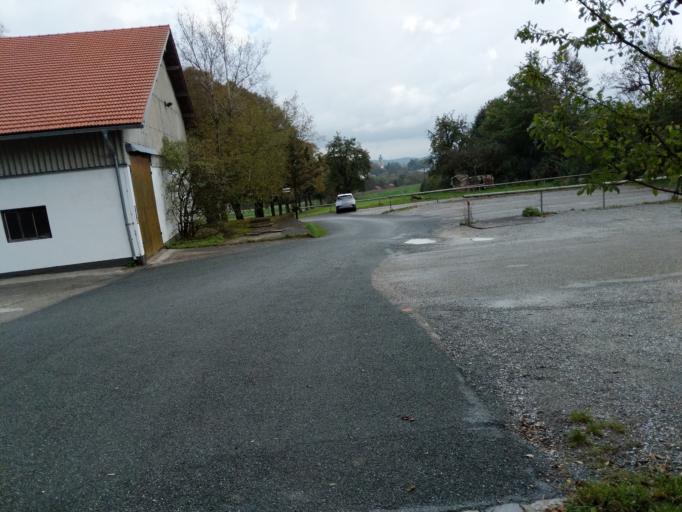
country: DE
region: Bavaria
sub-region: Upper Bavaria
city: Ebersberg
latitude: 48.0887
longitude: 11.9606
